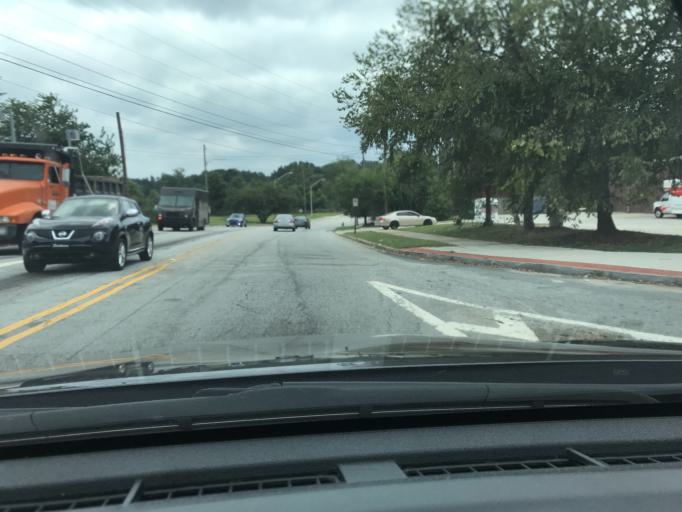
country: US
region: Georgia
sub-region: DeKalb County
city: Druid Hills
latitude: 33.7475
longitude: -84.3333
